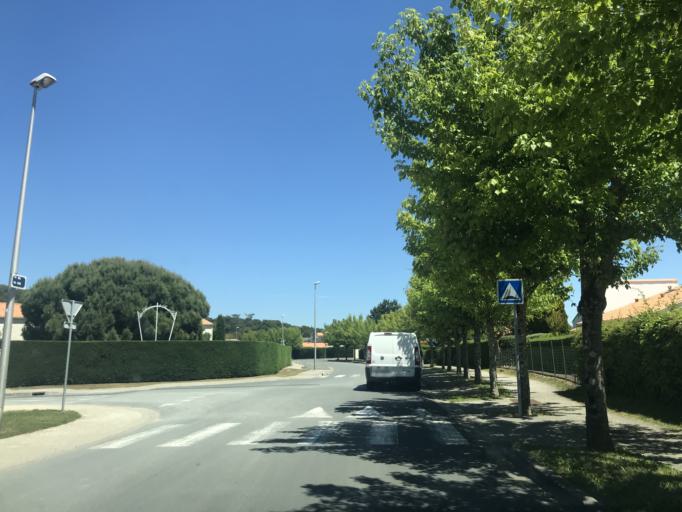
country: FR
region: Poitou-Charentes
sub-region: Departement de la Charente-Maritime
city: Saint-Palais-sur-Mer
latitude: 45.6509
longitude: -1.1077
